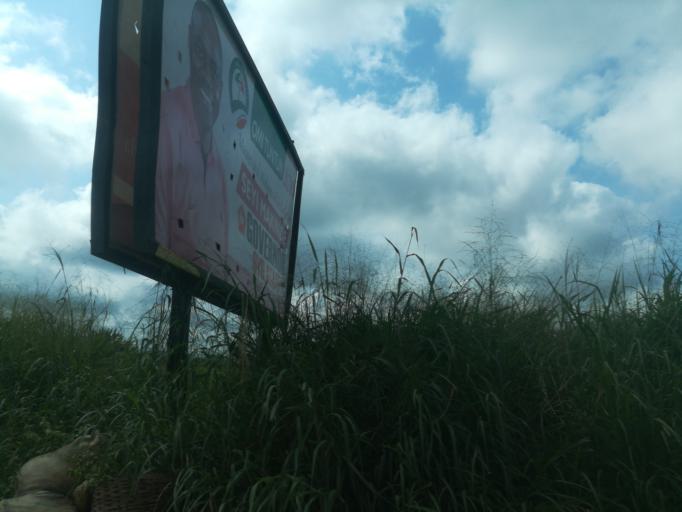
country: NG
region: Oyo
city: Ibadan
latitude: 7.3311
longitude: 3.8608
